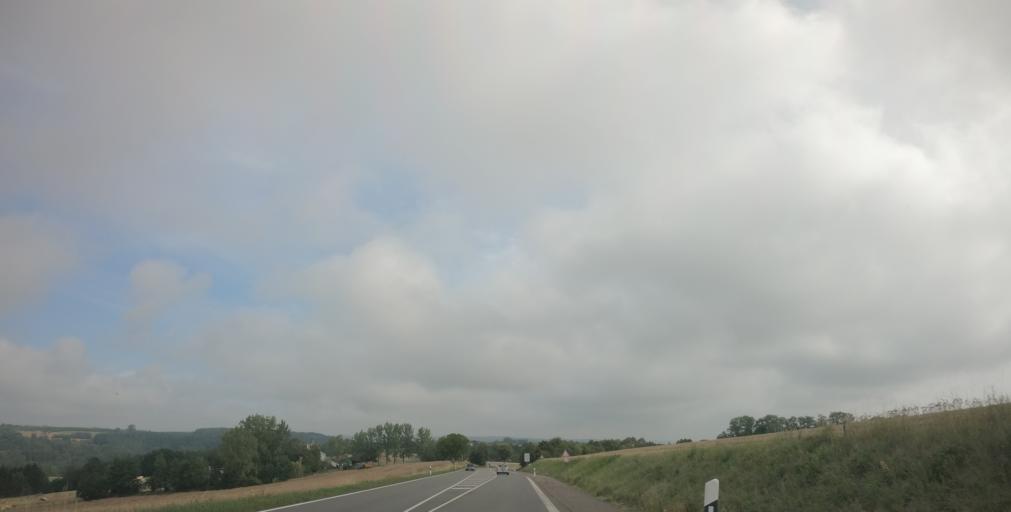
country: DE
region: Saarland
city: Blieskastel
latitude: 49.2282
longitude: 7.2375
